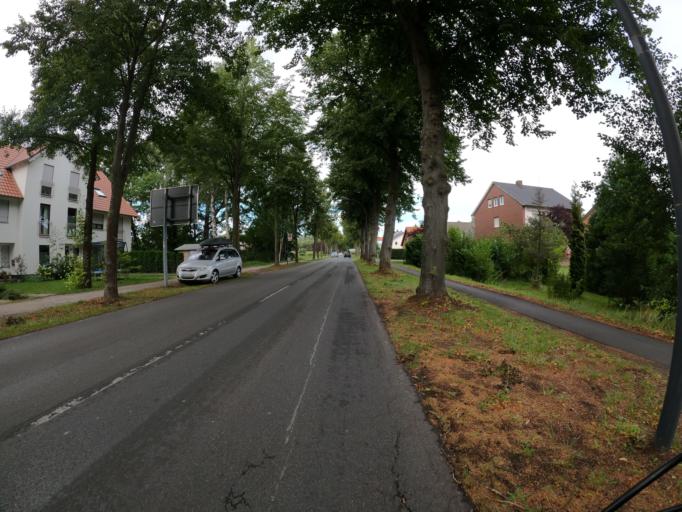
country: DE
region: North Rhine-Westphalia
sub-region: Regierungsbezirk Arnsberg
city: Lippstadt
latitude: 51.7061
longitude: 8.3385
